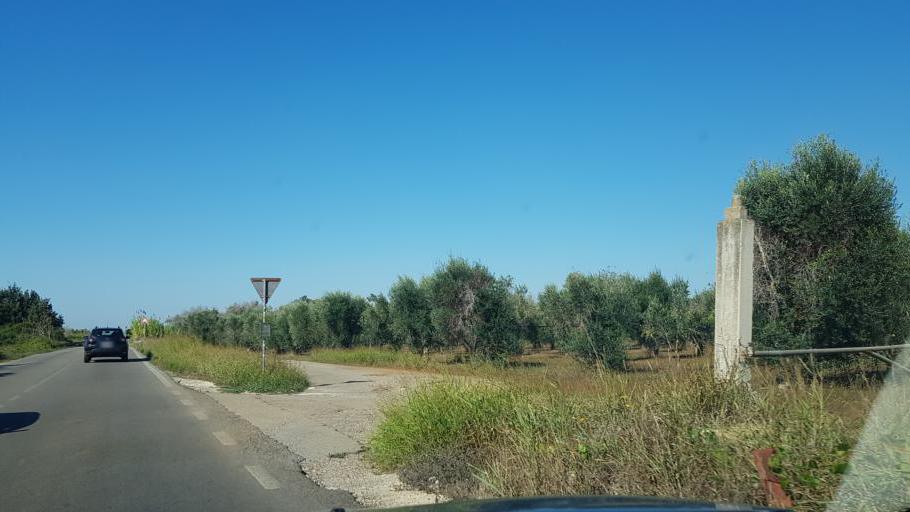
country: IT
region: Apulia
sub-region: Provincia di Lecce
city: Magliano
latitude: 40.3177
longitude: 18.0580
